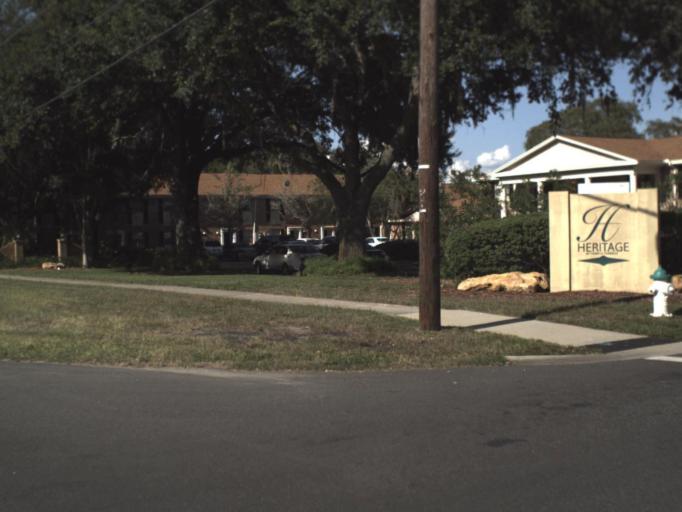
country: US
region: Florida
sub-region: Hillsborough County
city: Temple Terrace
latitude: 28.0449
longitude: -82.3935
